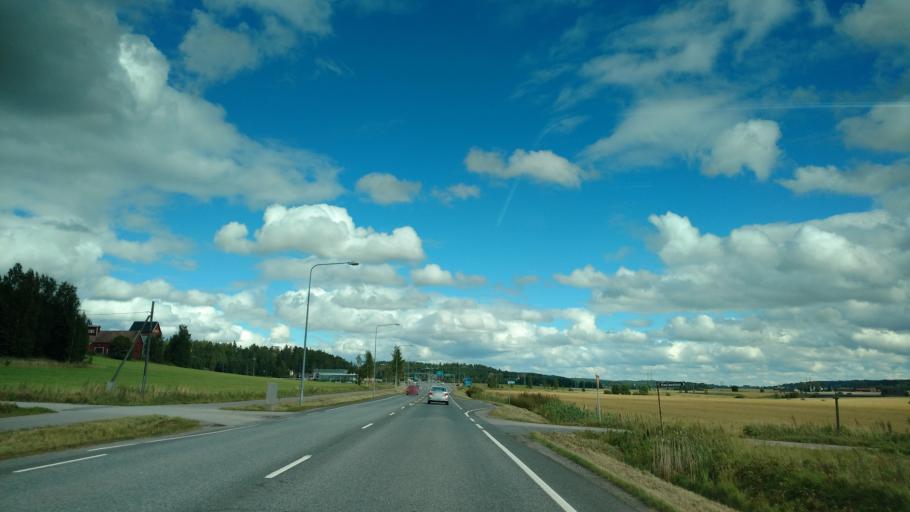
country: FI
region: Varsinais-Suomi
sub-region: Salo
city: Salo
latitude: 60.4126
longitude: 23.1601
